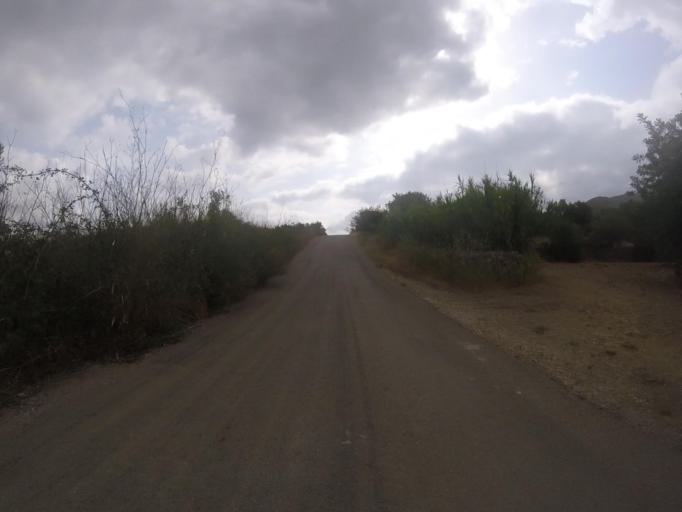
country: ES
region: Valencia
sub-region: Provincia de Castello
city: Santa Magdalena de Pulpis
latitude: 40.3514
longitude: 0.3017
